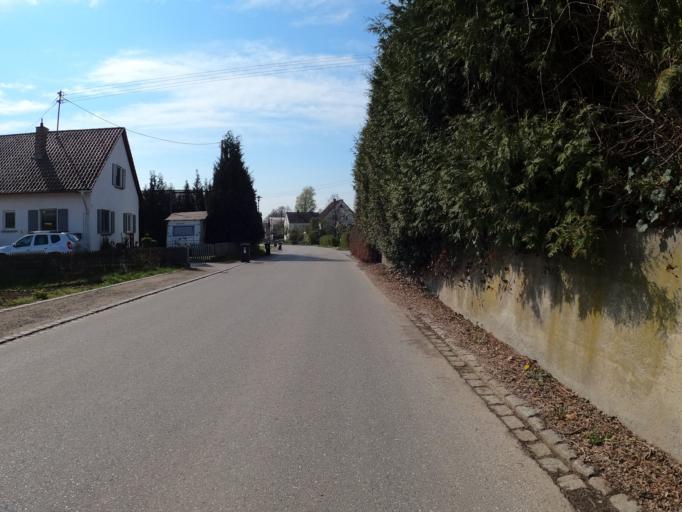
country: DE
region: Bavaria
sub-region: Swabia
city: Pfaffenhofen an der Roth
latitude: 48.3842
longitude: 10.1927
